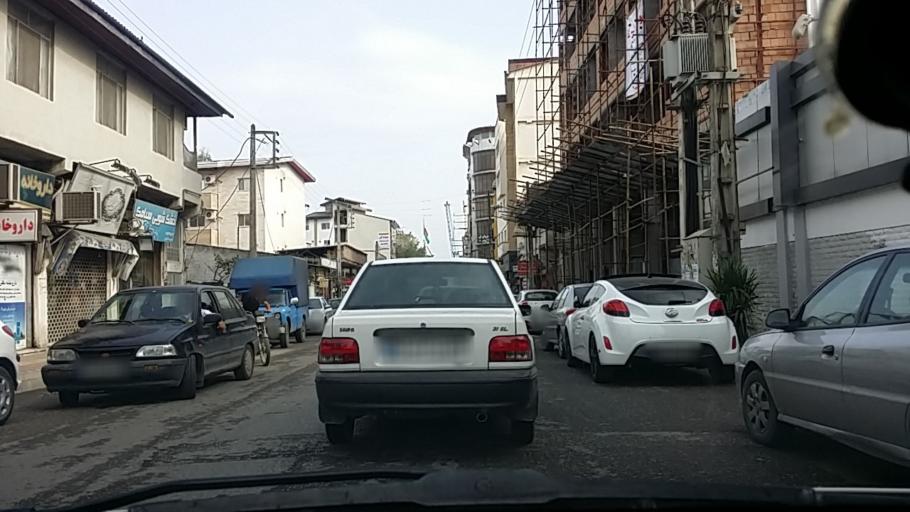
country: IR
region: Mazandaran
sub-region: Nowshahr
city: Nowshahr
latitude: 36.6493
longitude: 51.5087
